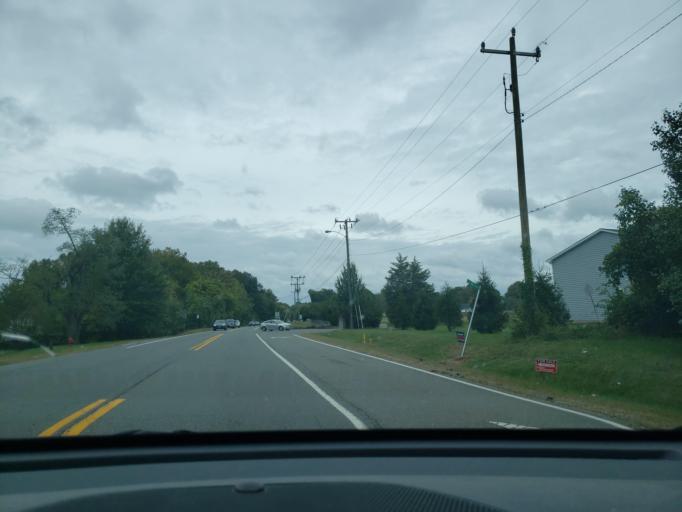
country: US
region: Virginia
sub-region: City of Fredericksburg
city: Fredericksburg
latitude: 38.2435
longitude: -77.4188
